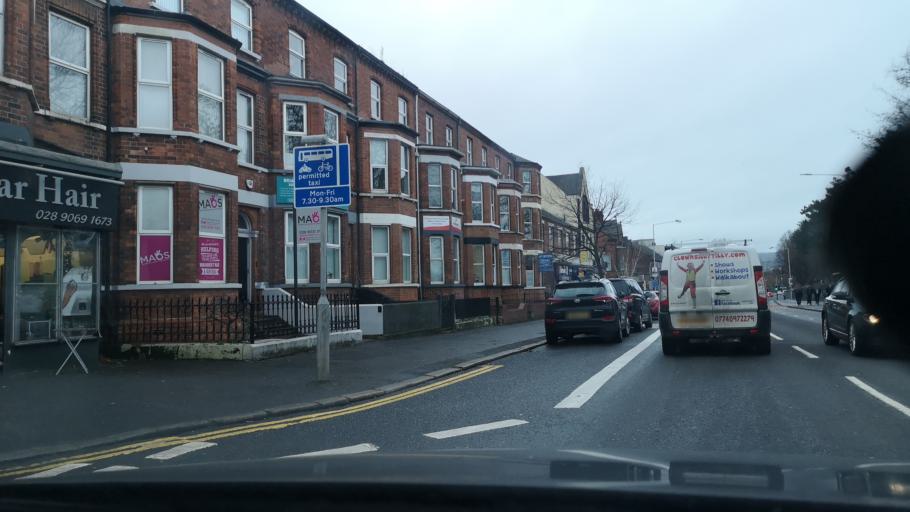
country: GB
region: Northern Ireland
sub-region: City of Belfast
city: Belfast
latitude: 54.5799
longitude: -5.9203
